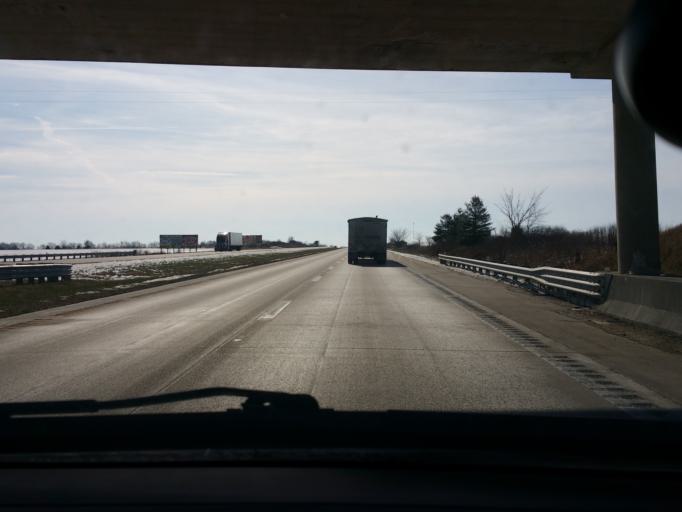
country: US
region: Missouri
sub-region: Clinton County
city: Cameron
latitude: 39.6329
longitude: -94.2444
